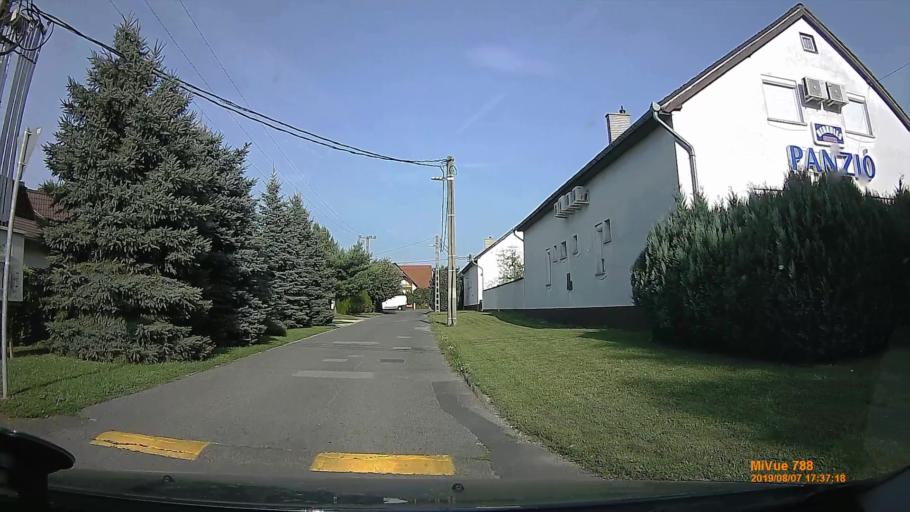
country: HU
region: Zala
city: Nagykanizsa
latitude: 46.4886
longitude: 16.9895
